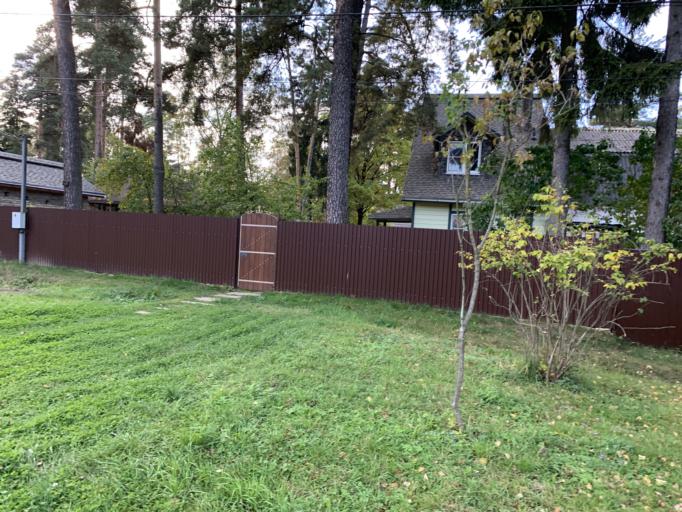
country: RU
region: Moskovskaya
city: Mamontovka
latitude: 55.9819
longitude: 37.8314
